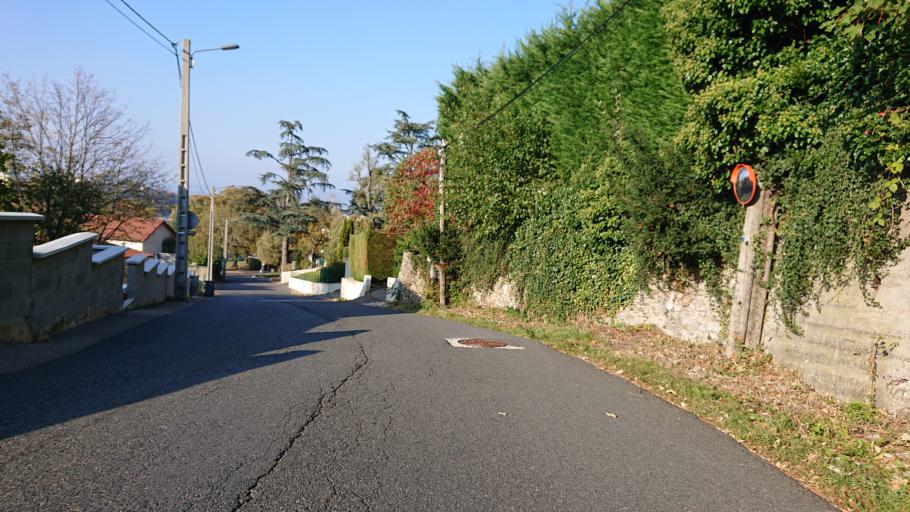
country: FR
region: Rhone-Alpes
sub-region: Departement de la Loire
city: Saint-Etienne
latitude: 45.4196
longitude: 4.4274
